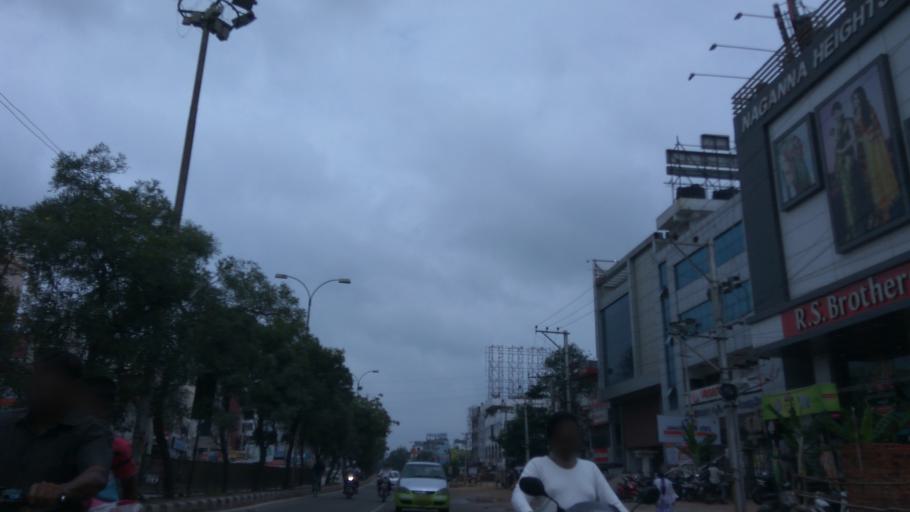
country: IN
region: Telangana
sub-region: Rangareddi
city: Secunderabad
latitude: 17.4774
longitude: 78.5633
